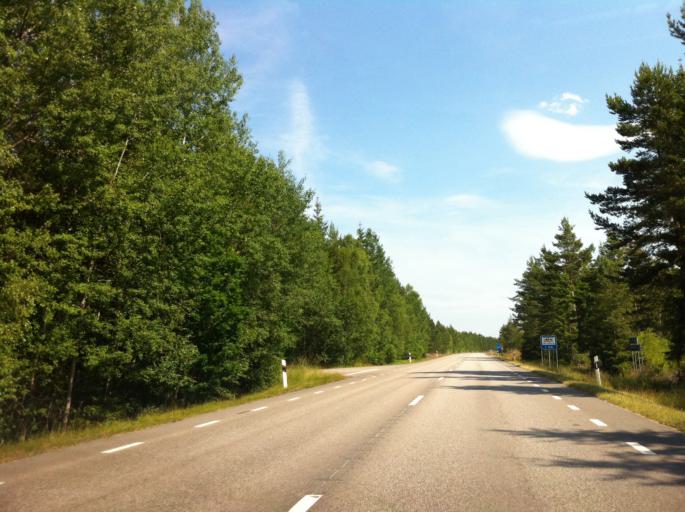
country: SE
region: Kalmar
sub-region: Nybro Kommun
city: Nybro
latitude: 56.8387
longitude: 15.7234
